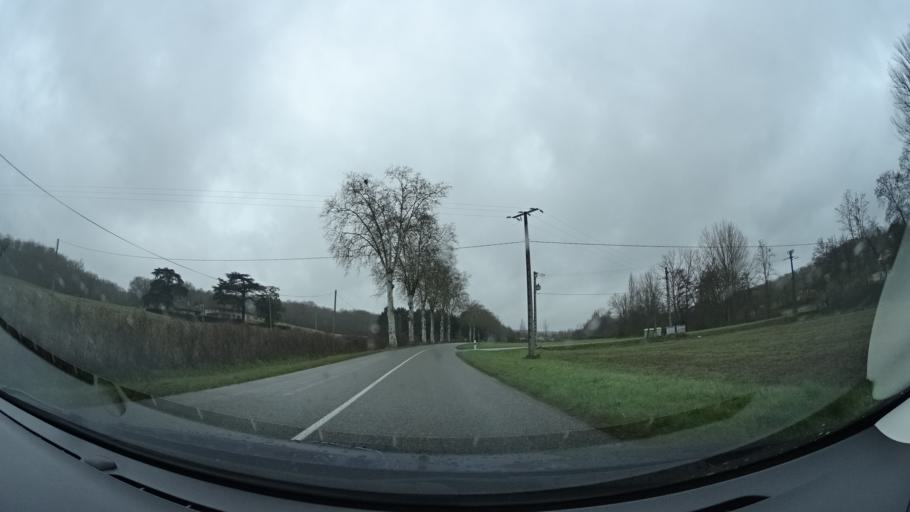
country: FR
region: Midi-Pyrenees
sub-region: Departement du Tarn-et-Garonne
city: Moissac
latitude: 44.1345
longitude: 1.1011
